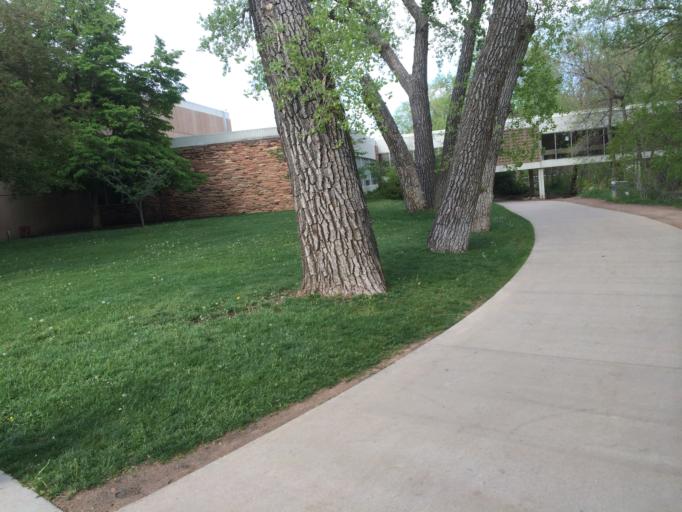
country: US
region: Colorado
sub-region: Boulder County
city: Boulder
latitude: 40.0145
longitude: -105.2828
